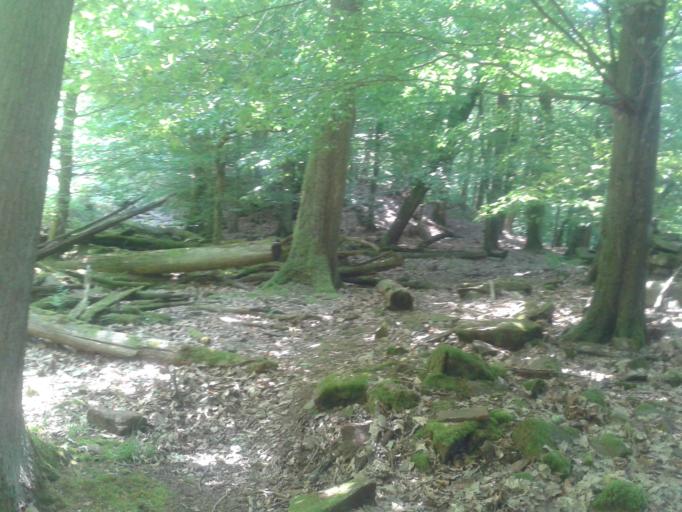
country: DE
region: Baden-Wuerttemberg
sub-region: Karlsruhe Region
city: Neckargemund
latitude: 49.4080
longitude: 8.7815
